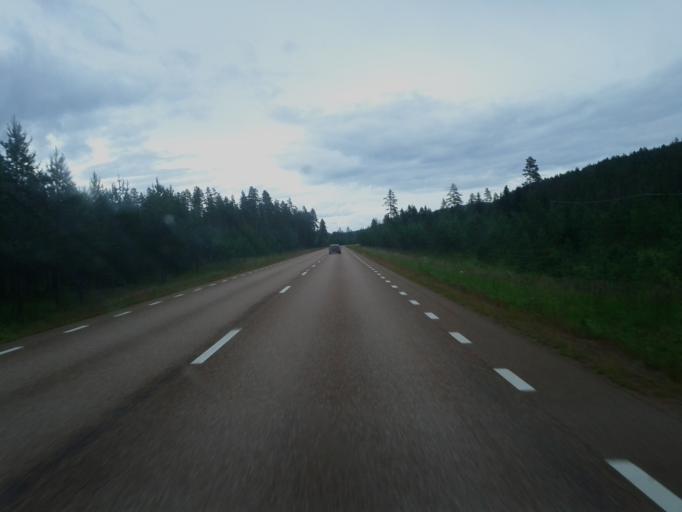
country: SE
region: Dalarna
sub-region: Alvdalens Kommun
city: AElvdalen
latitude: 61.2781
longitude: 13.8753
